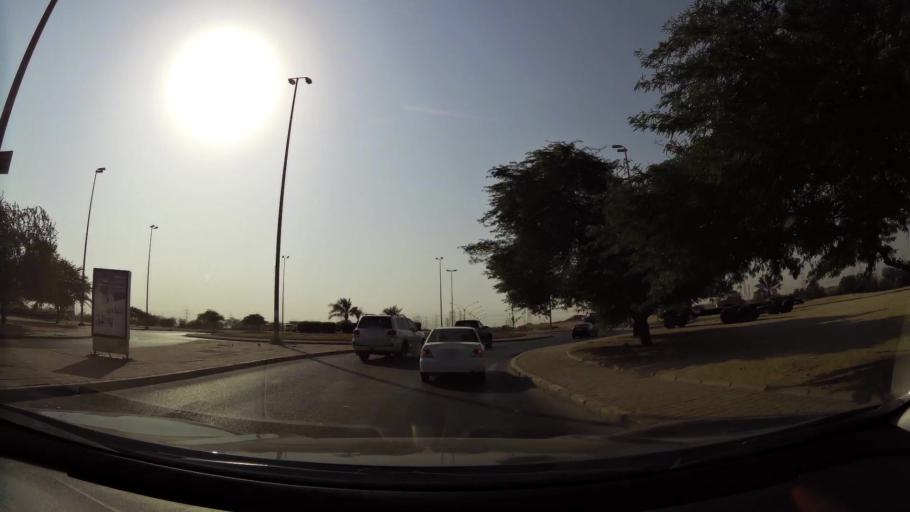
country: KW
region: Al Ahmadi
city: Ar Riqqah
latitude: 29.1528
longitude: 48.0718
